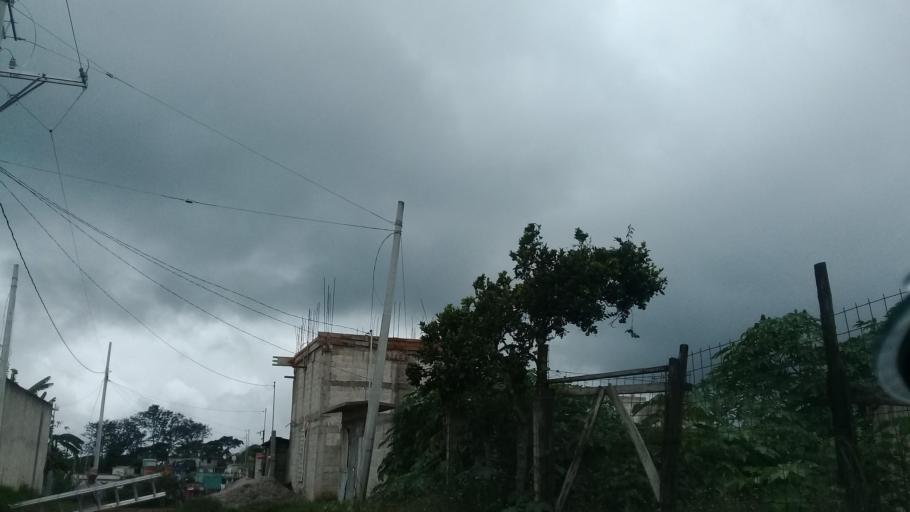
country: MX
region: Veracruz
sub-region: Emiliano Zapata
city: Las Trancas
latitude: 19.4961
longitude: -96.8660
